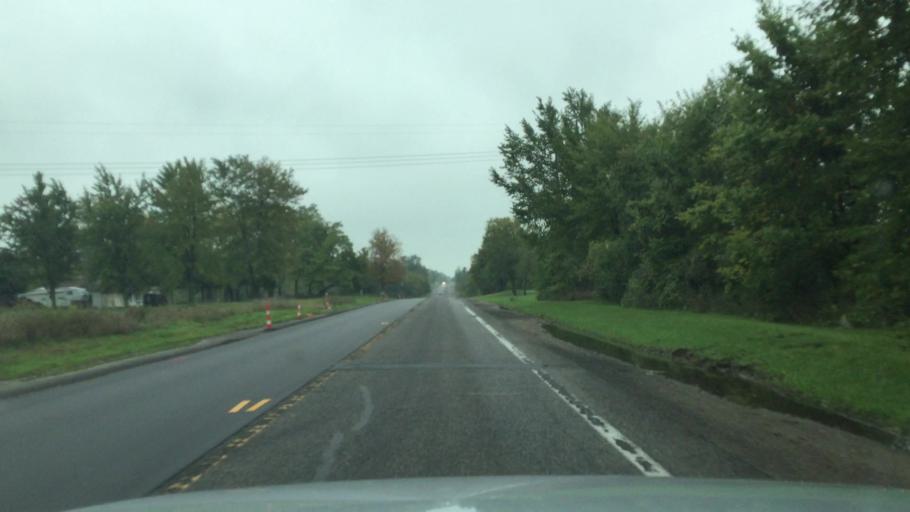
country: US
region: Michigan
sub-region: Shiawassee County
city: Perry
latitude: 42.9164
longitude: -84.2224
